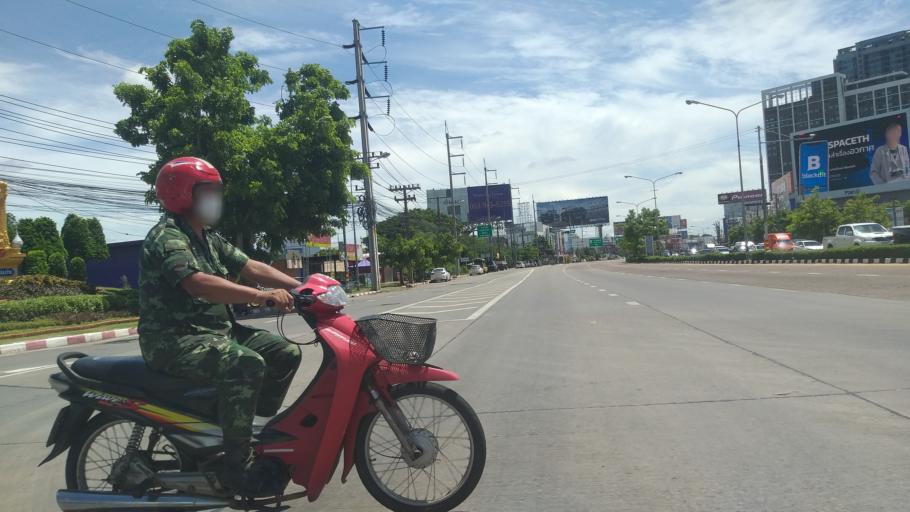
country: TH
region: Khon Kaen
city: Khon Kaen
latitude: 16.4321
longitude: 102.8235
